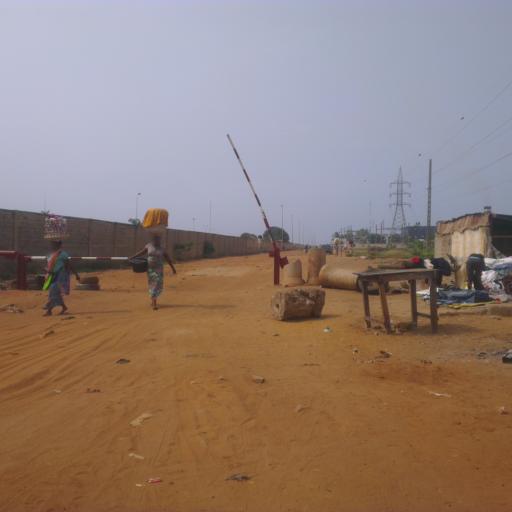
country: TG
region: Maritime
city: Lome
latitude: 6.1636
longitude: 1.3025
